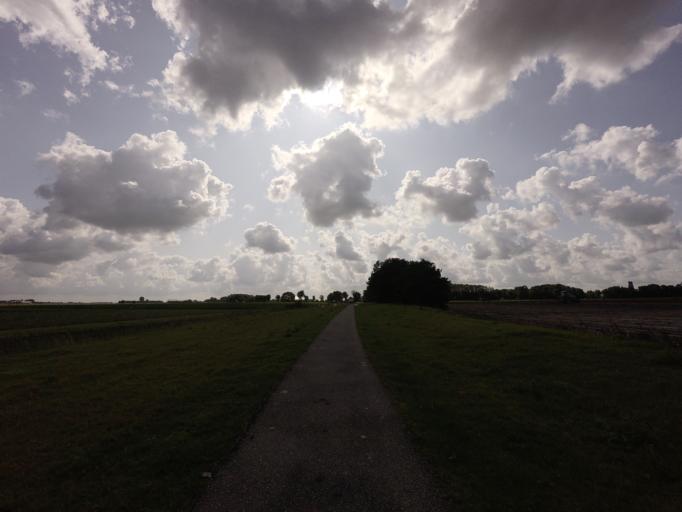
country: NL
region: Friesland
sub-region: Gemeente Het Bildt
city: Minnertsga
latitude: 53.2605
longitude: 5.5948
